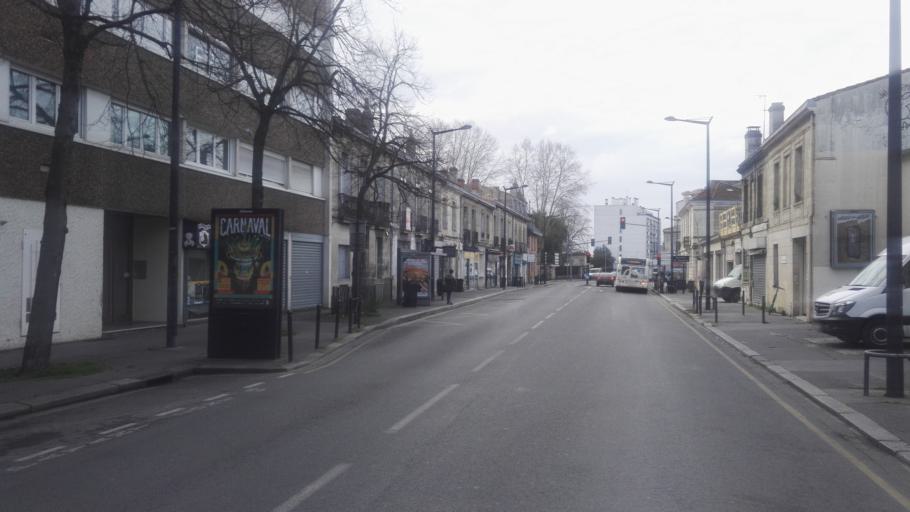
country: FR
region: Aquitaine
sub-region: Departement de la Gironde
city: Begles
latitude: 44.8157
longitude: -0.5724
